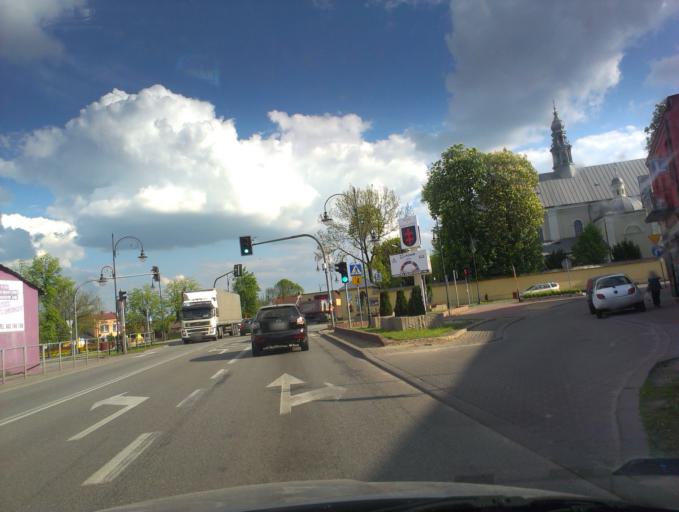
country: PL
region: Masovian Voivodeship
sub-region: Powiat radomski
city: Skaryszew
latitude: 51.3110
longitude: 21.2520
